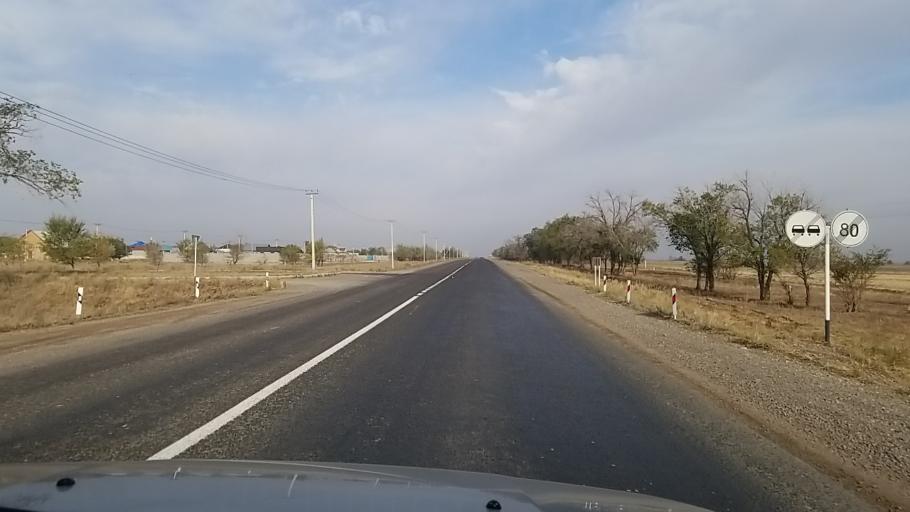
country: KZ
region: Almaty Oblysy
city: Burunday
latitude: 43.4803
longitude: 76.6777
